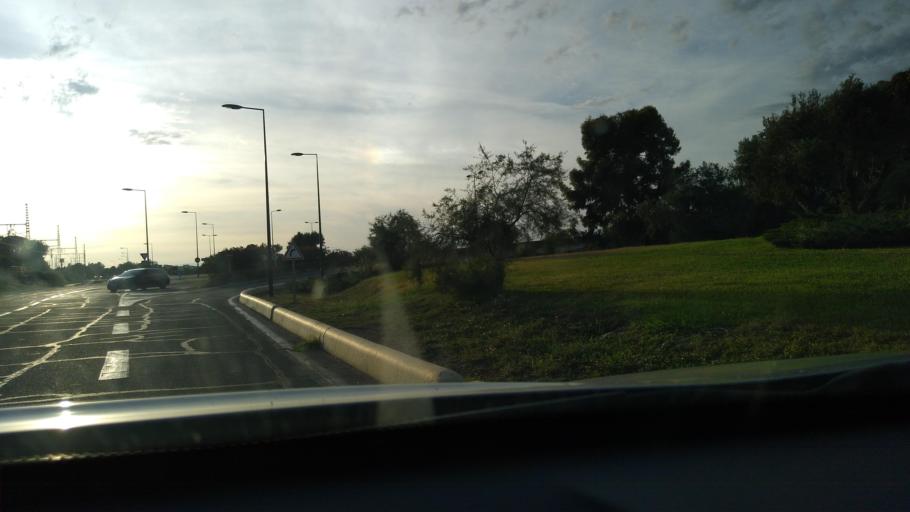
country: FR
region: Languedoc-Roussillon
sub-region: Departement de l'Herault
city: Sete
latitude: 43.4133
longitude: 3.6841
